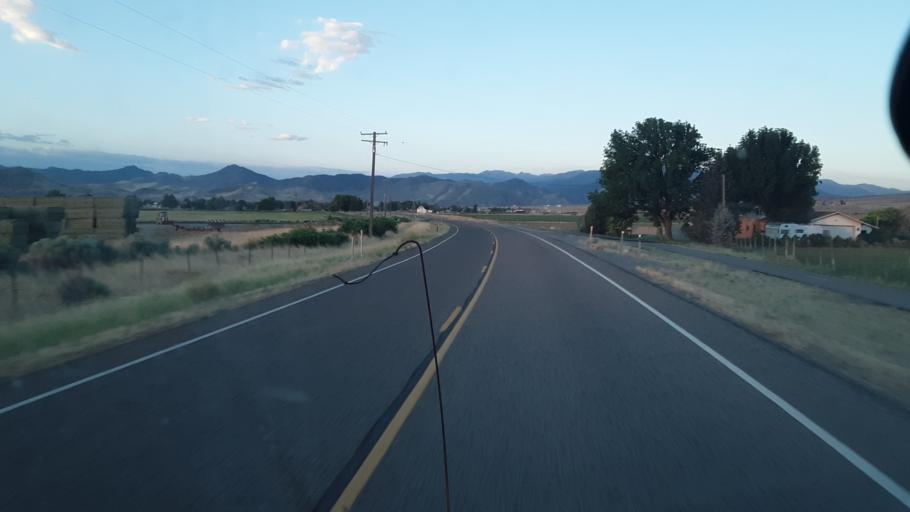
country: US
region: Utah
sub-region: Sevier County
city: Monroe
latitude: 38.6405
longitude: -112.2158
